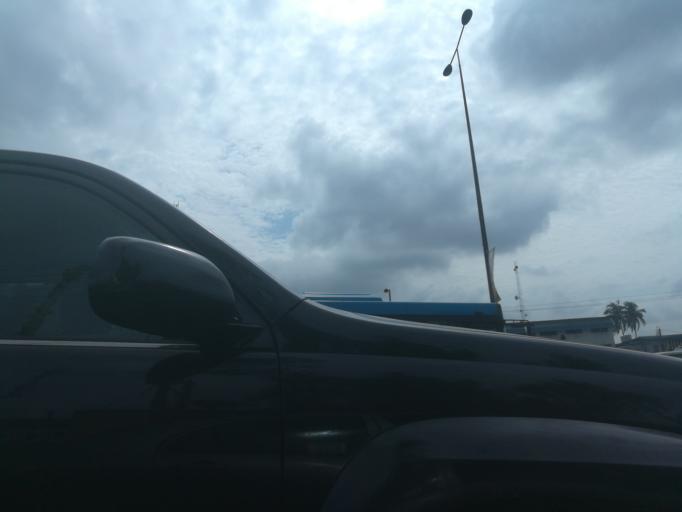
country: NG
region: Lagos
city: Somolu
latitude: 6.5618
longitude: 3.3665
